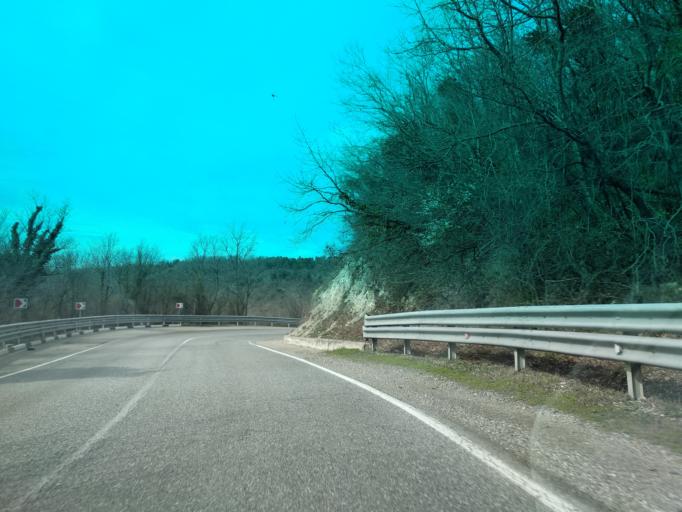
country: RU
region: Krasnodarskiy
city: Shepsi
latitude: 44.0517
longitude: 39.1314
